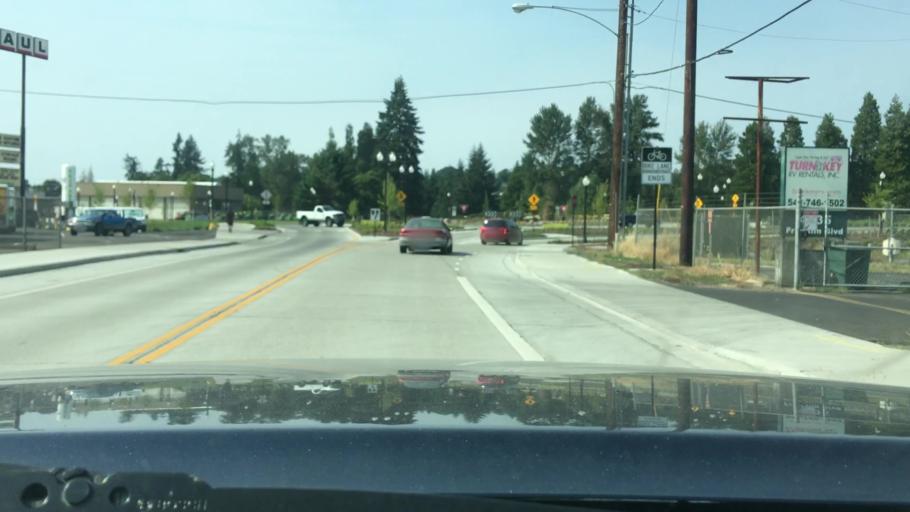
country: US
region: Oregon
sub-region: Lane County
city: Springfield
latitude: 44.0433
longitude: -123.0300
